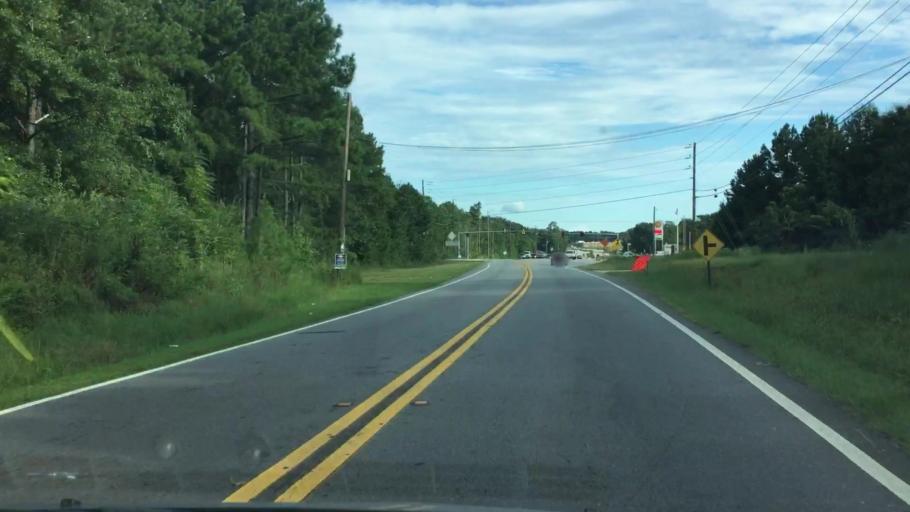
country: US
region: Georgia
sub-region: Clayton County
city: Conley
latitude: 33.6278
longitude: -84.2575
